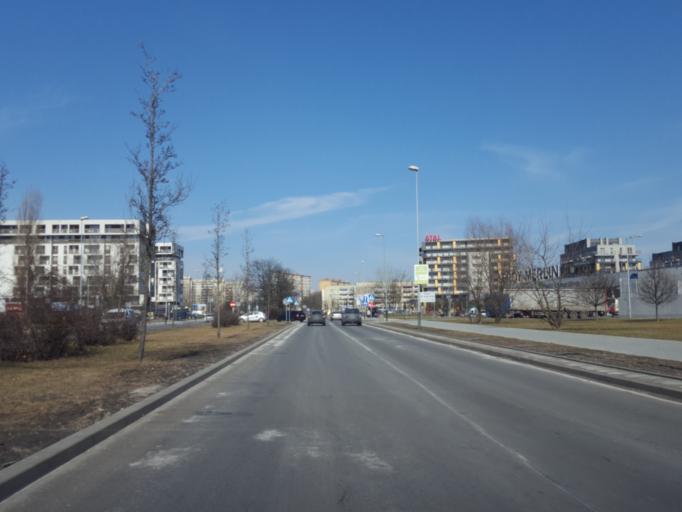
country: PL
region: Lesser Poland Voivodeship
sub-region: Krakow
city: Krakow
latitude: 50.0769
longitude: 20.0141
